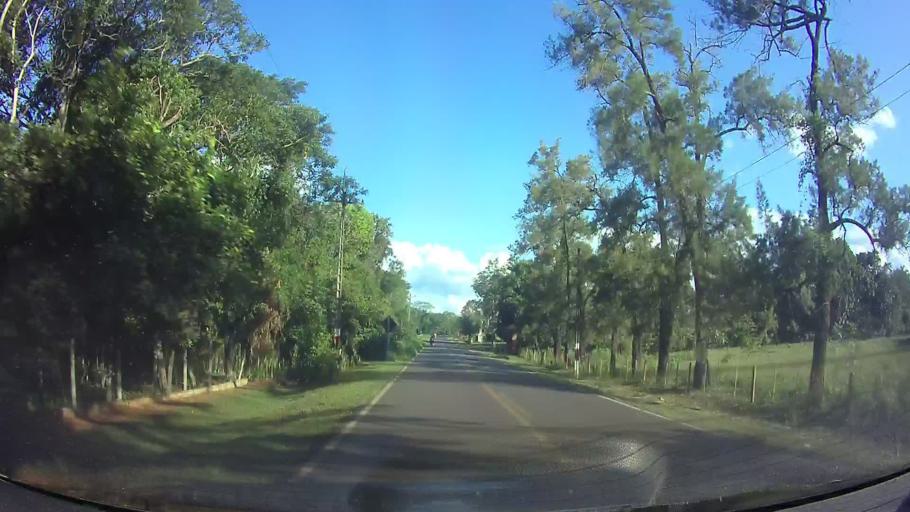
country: PY
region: Central
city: Aregua
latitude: -25.3298
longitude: -57.3851
